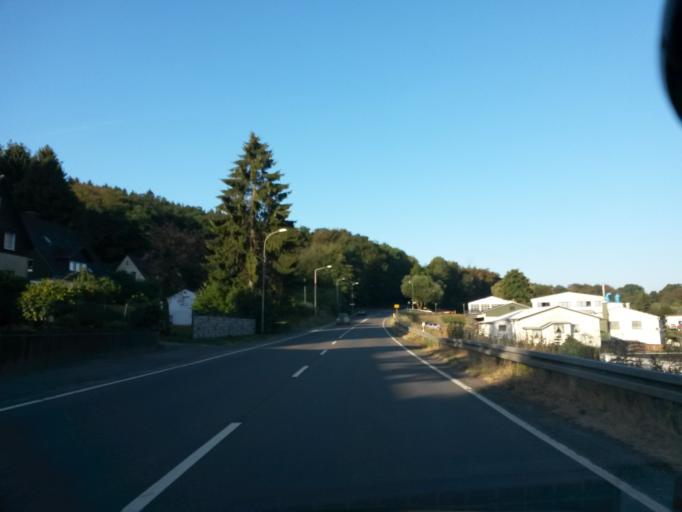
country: DE
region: North Rhine-Westphalia
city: Kierspe
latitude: 51.1214
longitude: 7.5946
